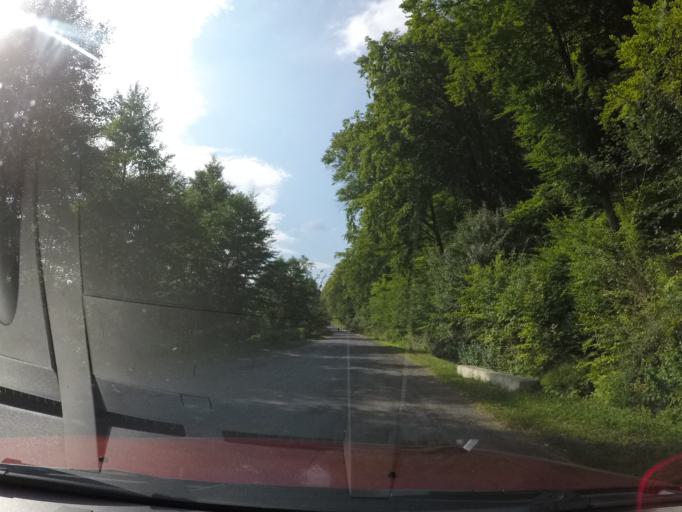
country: UA
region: Zakarpattia
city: Velykyi Bereznyi
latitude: 48.9208
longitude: 22.4555
